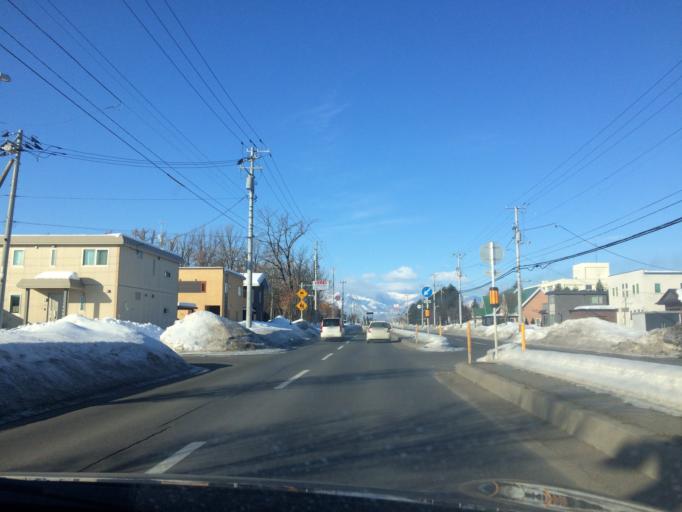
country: JP
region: Hokkaido
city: Obihiro
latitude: 42.9128
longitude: 143.0751
